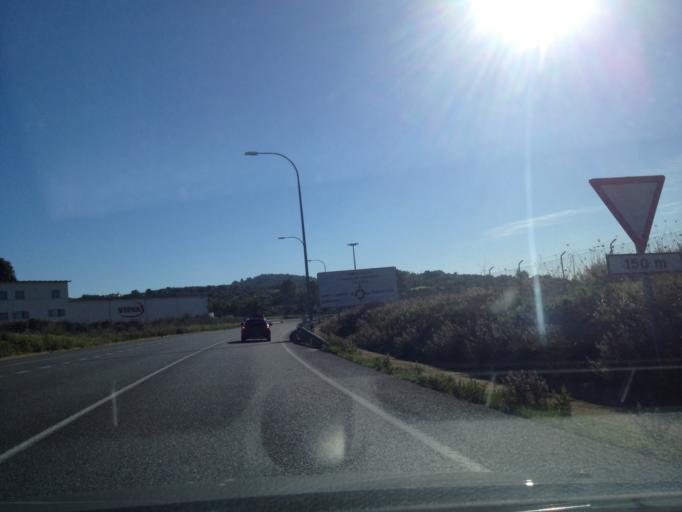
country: ES
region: Balearic Islands
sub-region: Illes Balears
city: Manacor
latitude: 39.5854
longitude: 3.2309
